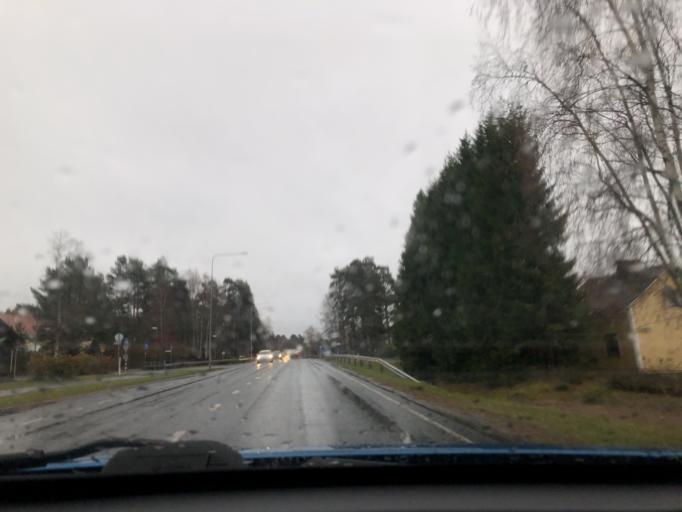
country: FI
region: Pirkanmaa
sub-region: Tampere
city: Kangasala
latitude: 61.4705
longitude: 24.0349
